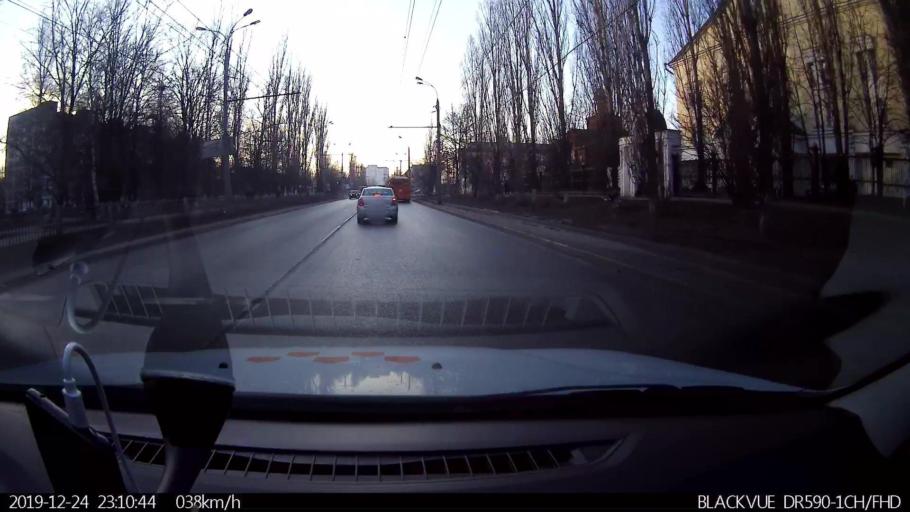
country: RU
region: Nizjnij Novgorod
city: Gorbatovka
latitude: 56.2621
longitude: 43.8801
